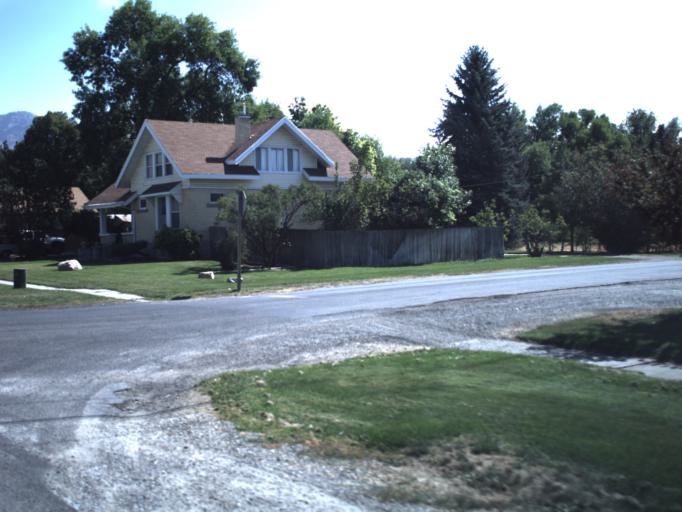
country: US
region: Utah
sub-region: Cache County
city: Smithfield
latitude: 41.8387
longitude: -111.8385
